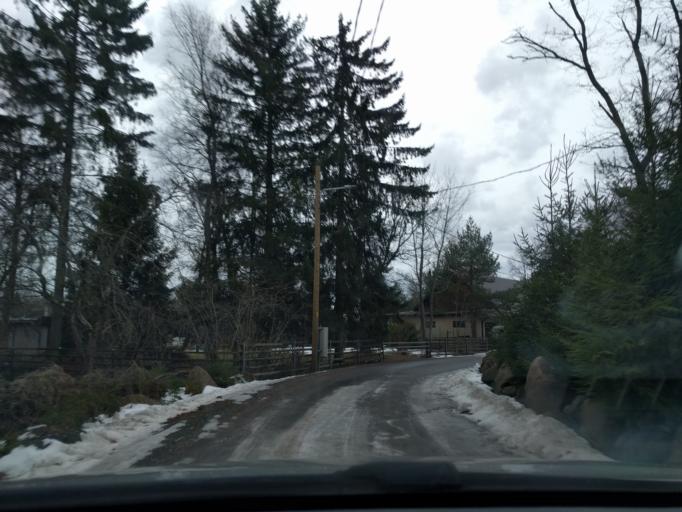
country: EE
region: Harju
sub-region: Viimsi vald
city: Viimsi
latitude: 59.5161
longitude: 24.9060
